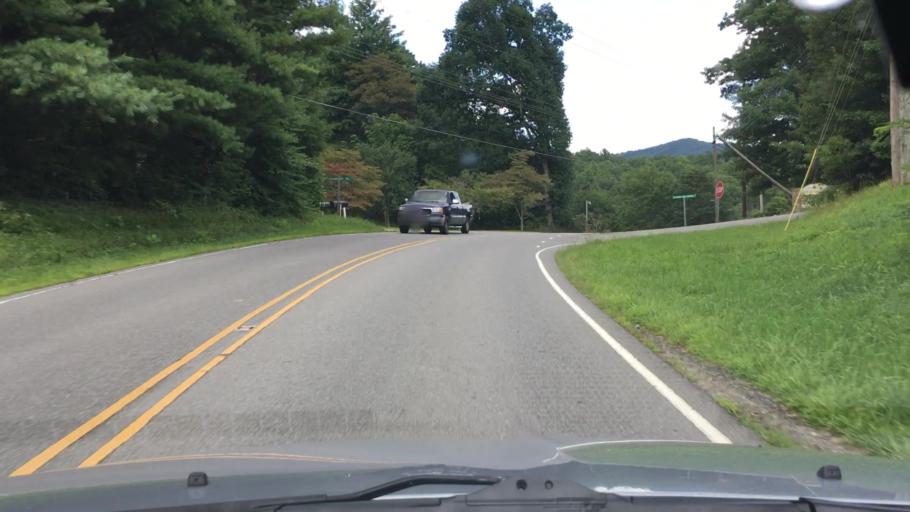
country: US
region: North Carolina
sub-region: Yancey County
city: Burnsville
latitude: 35.8381
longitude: -82.1893
